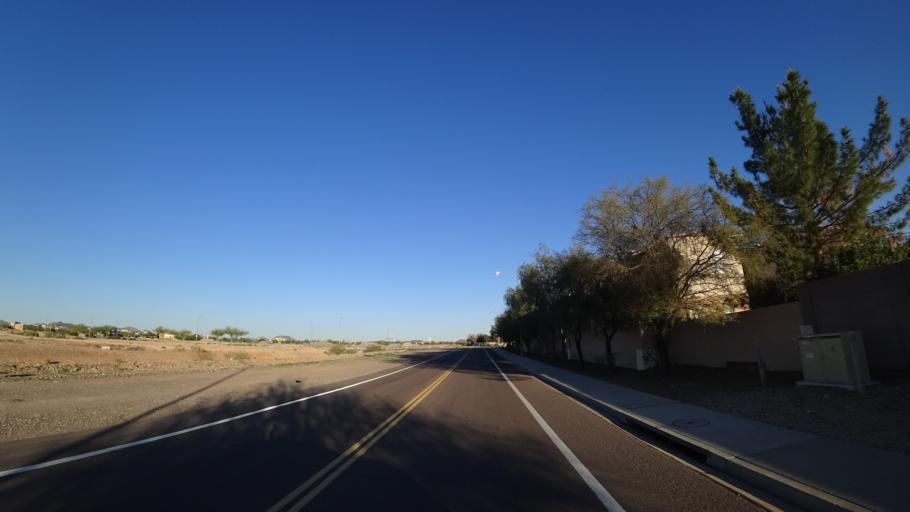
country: US
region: Arizona
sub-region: Maricopa County
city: Sun City West
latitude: 33.6744
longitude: -112.2814
